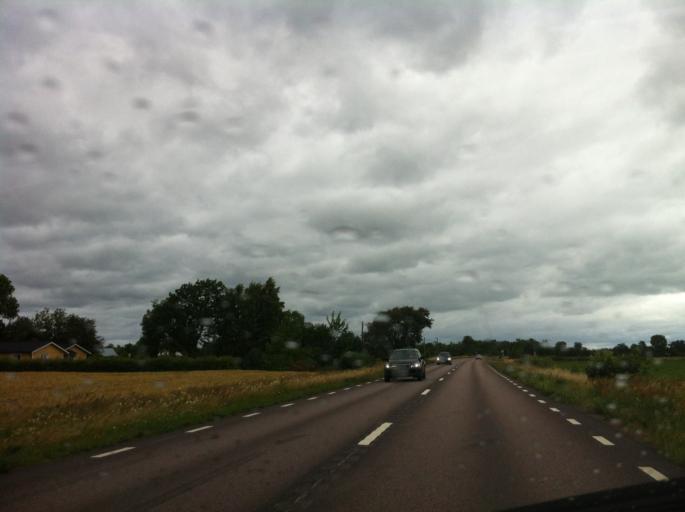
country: SE
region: Kalmar
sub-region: Borgholms Kommun
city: Borgholm
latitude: 57.1280
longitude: 16.9712
